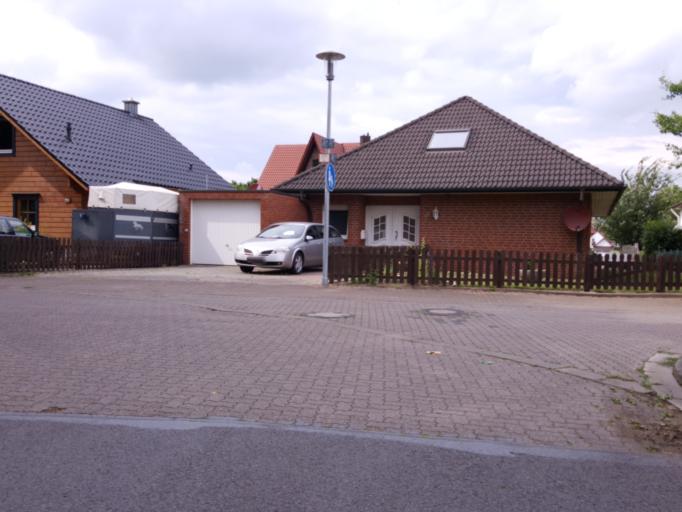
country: DE
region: North Rhine-Westphalia
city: Bad Oeynhausen
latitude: 52.2115
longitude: 8.8227
